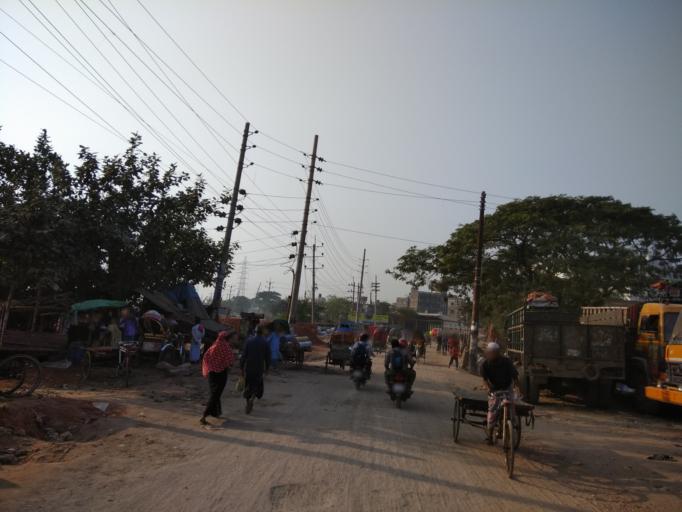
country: BD
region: Dhaka
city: Azimpur
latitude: 23.7138
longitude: 90.3840
